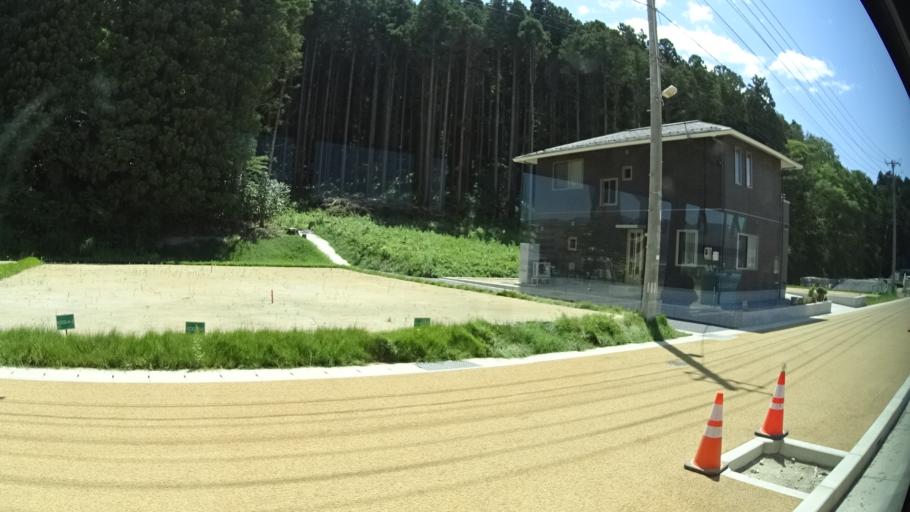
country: JP
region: Iwate
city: Ofunato
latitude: 39.0202
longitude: 141.6355
